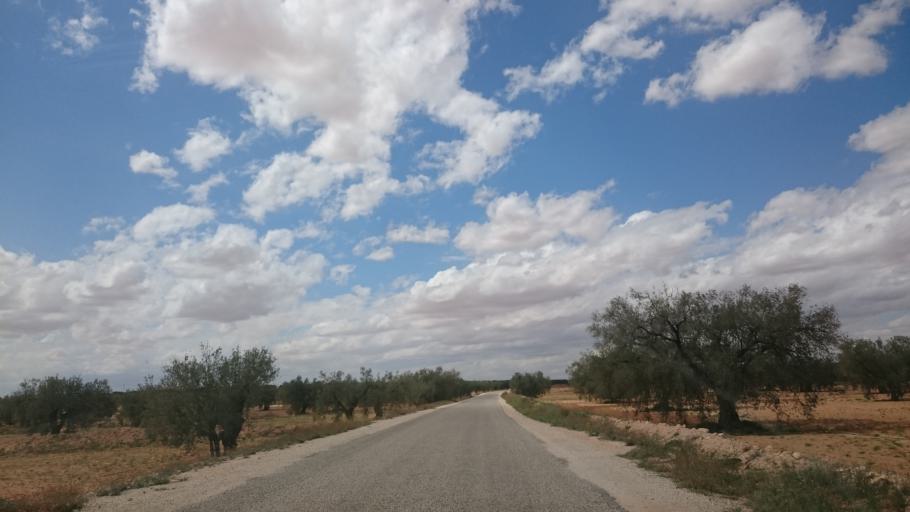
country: TN
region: Safaqis
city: Bi'r `Ali Bin Khalifah
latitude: 34.7919
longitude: 10.3349
